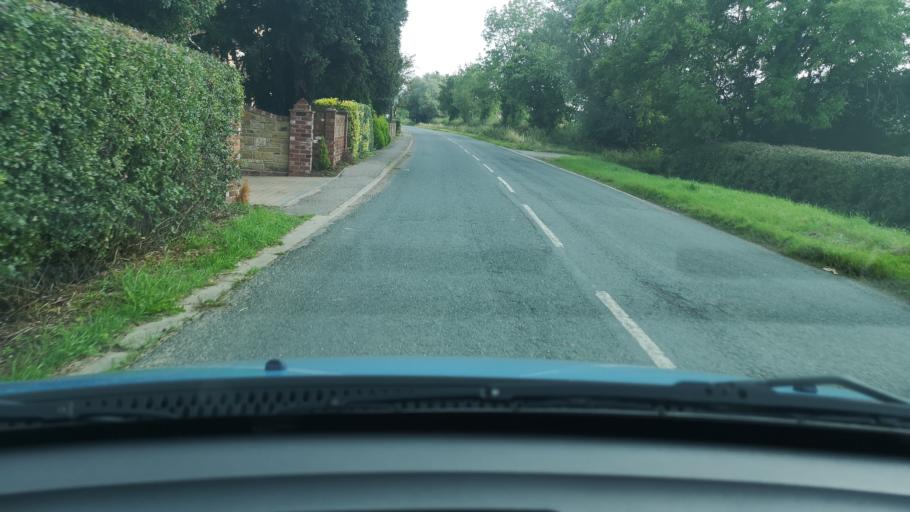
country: GB
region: England
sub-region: East Riding of Yorkshire
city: Pollington
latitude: 53.6408
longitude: -1.0544
